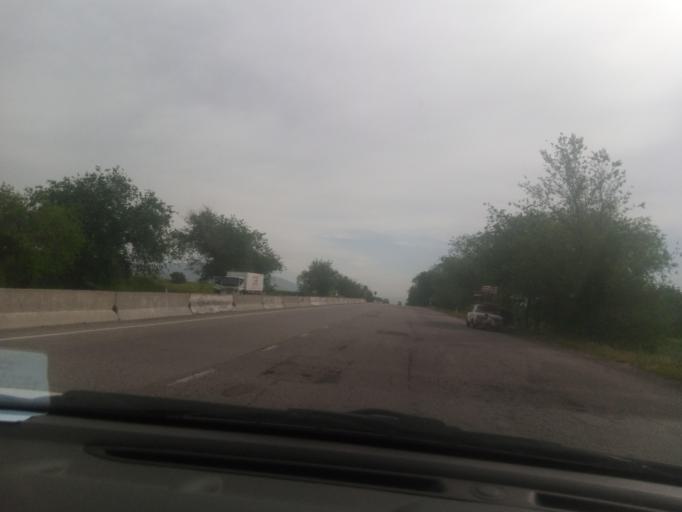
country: UZ
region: Toshkent
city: Angren
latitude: 40.9563
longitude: 69.9317
